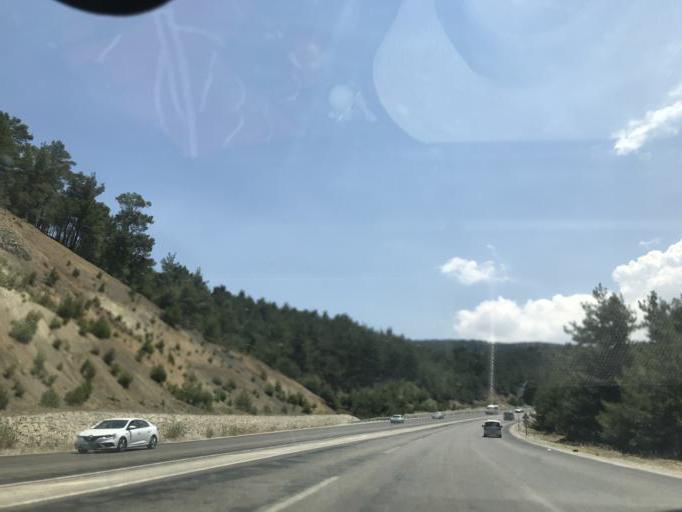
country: TR
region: Denizli
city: Serinhisar
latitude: 37.6647
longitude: 29.2295
